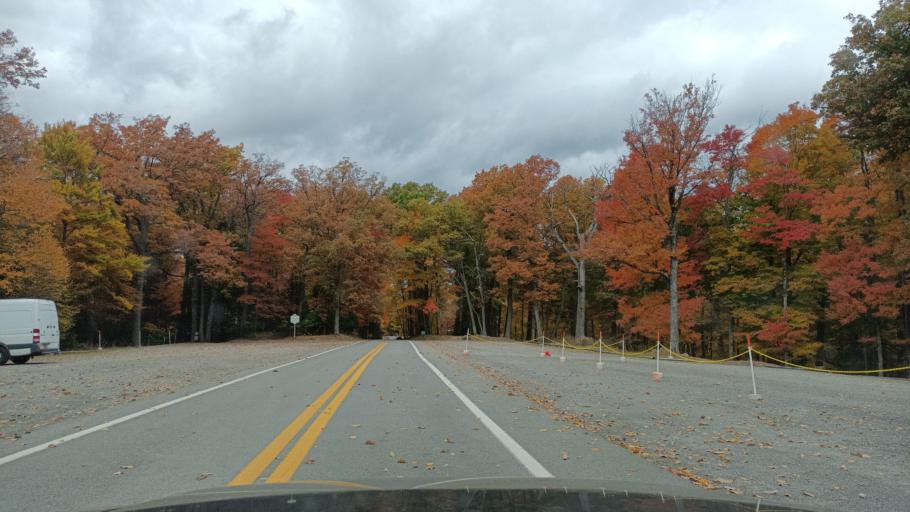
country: US
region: West Virginia
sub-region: Monongalia County
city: Cheat Lake
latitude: 39.6366
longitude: -79.8128
